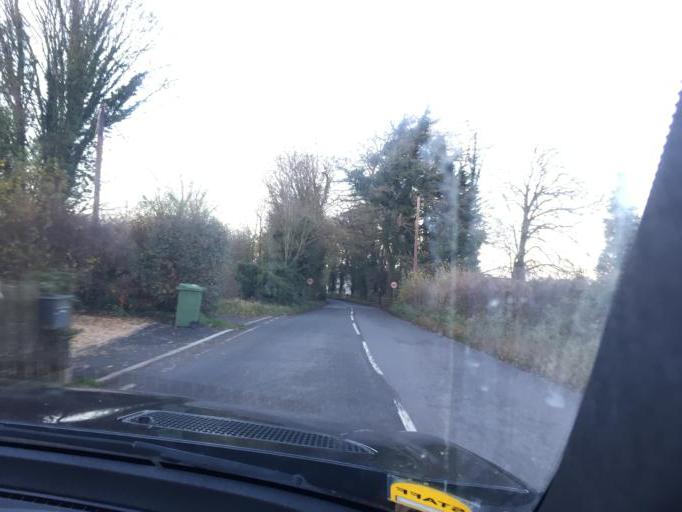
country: GB
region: England
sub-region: Northamptonshire
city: Brackley
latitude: 52.0837
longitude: -1.1456
